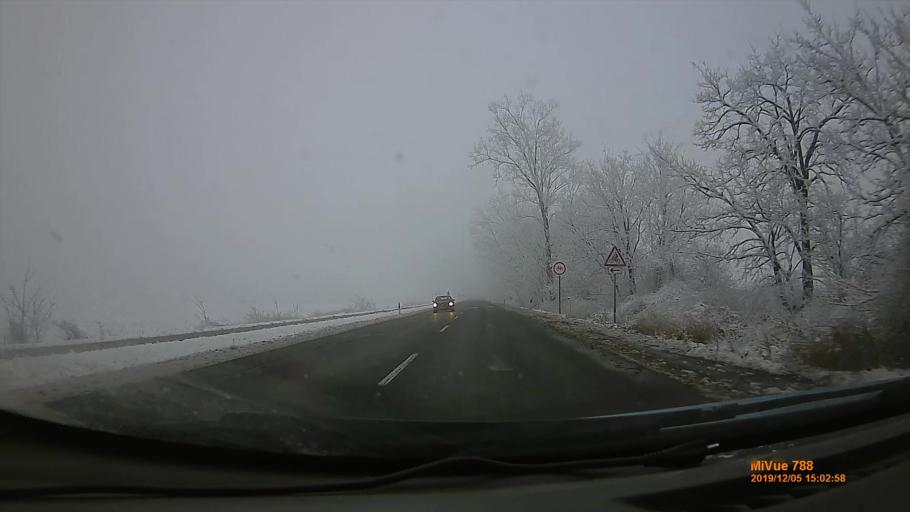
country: HU
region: Szabolcs-Szatmar-Bereg
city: Tiszanagyfalu
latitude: 48.0806
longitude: 21.5057
